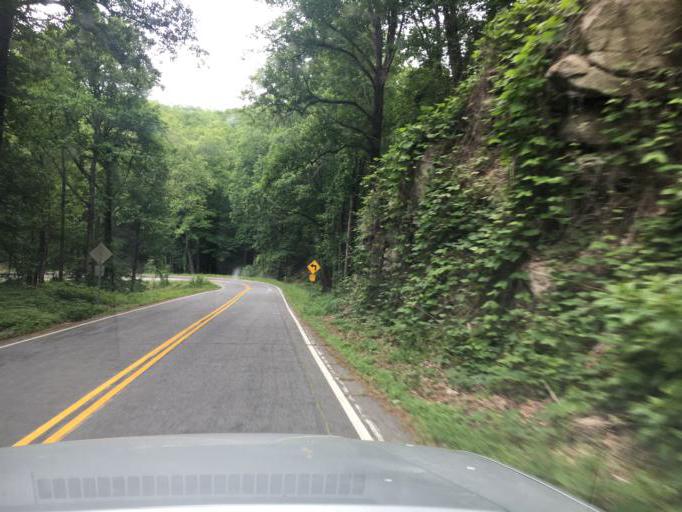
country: US
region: South Carolina
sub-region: Greenville County
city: Tigerville
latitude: 35.1653
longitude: -82.4143
